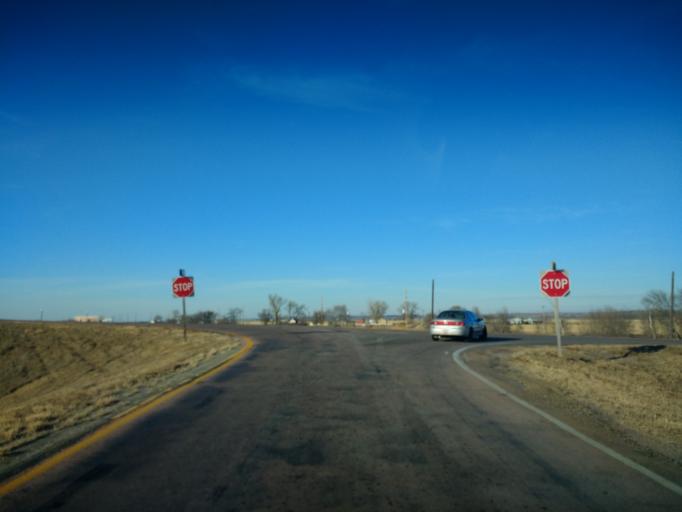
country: US
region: South Dakota
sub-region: Union County
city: North Sioux City
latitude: 42.5499
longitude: -96.5075
